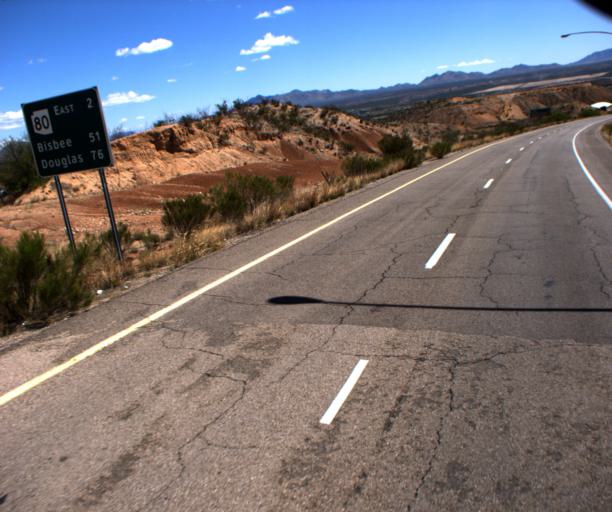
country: US
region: Arizona
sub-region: Cochise County
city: Whetstone
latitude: 31.9712
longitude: -110.3262
